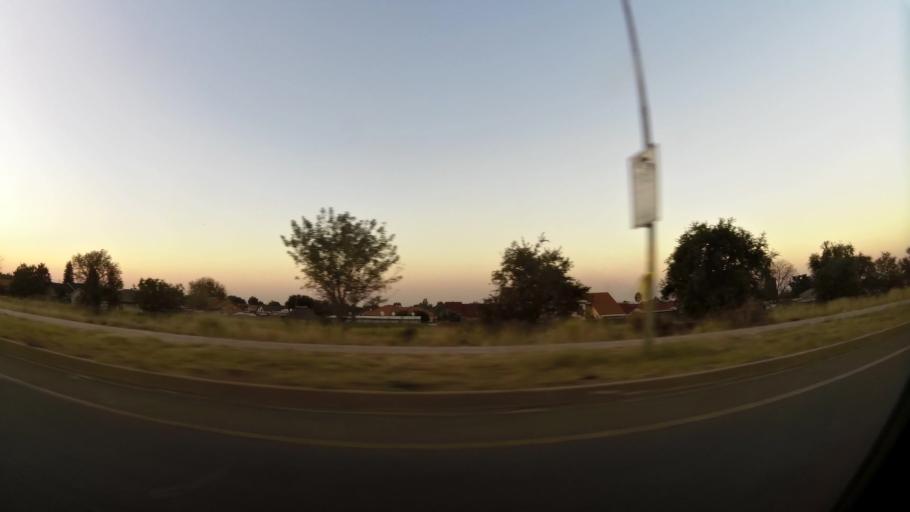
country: ZA
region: North-West
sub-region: Bojanala Platinum District Municipality
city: Rustenburg
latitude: -25.6441
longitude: 27.2078
